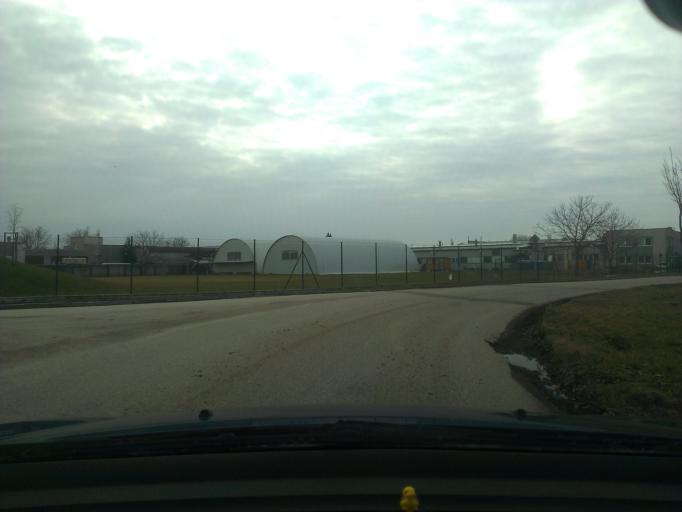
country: SK
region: Trnavsky
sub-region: Okres Trnava
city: Piestany
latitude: 48.6007
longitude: 17.8160
